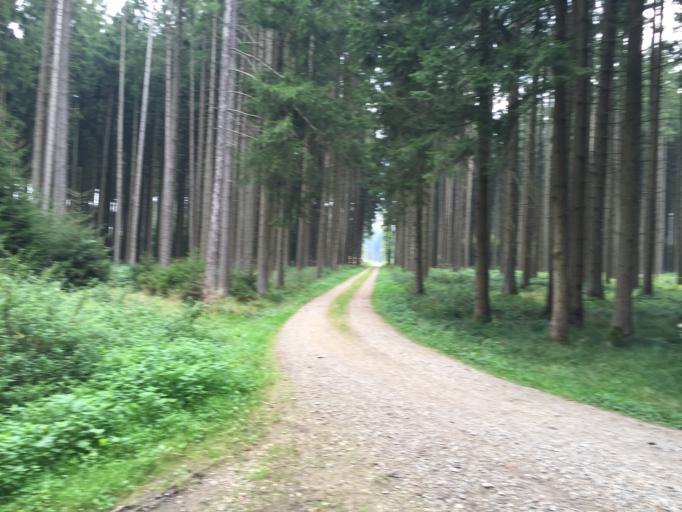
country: DE
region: Baden-Wuerttemberg
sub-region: Tuebingen Region
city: Burgrieden
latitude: 48.2046
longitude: 9.9268
